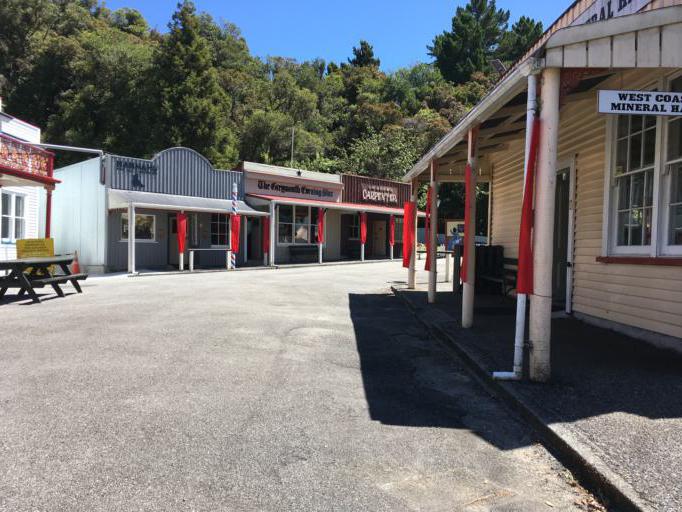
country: NZ
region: West Coast
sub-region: Grey District
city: Greymouth
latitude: -42.5356
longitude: 171.1818
